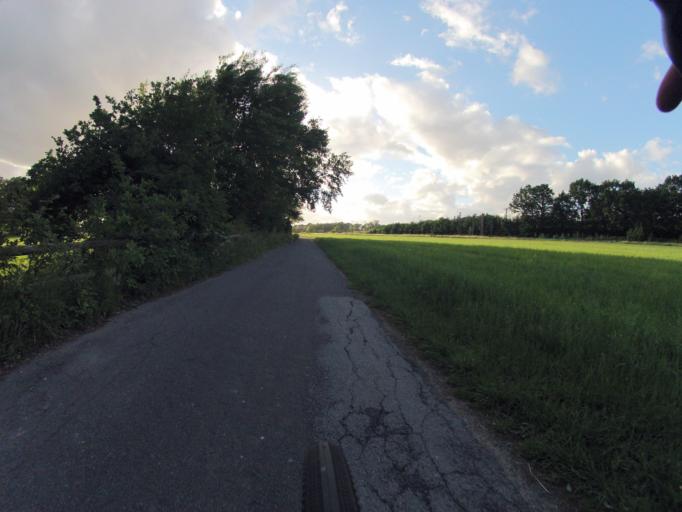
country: DE
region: North Rhine-Westphalia
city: Ibbenburen
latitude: 52.2934
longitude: 7.6785
